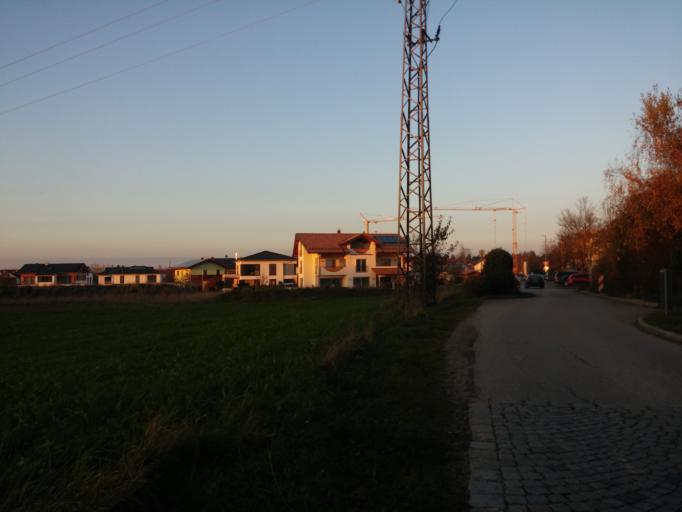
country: DE
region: Bavaria
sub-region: Upper Bavaria
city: Kirchseeon
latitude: 48.0771
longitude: 11.8581
